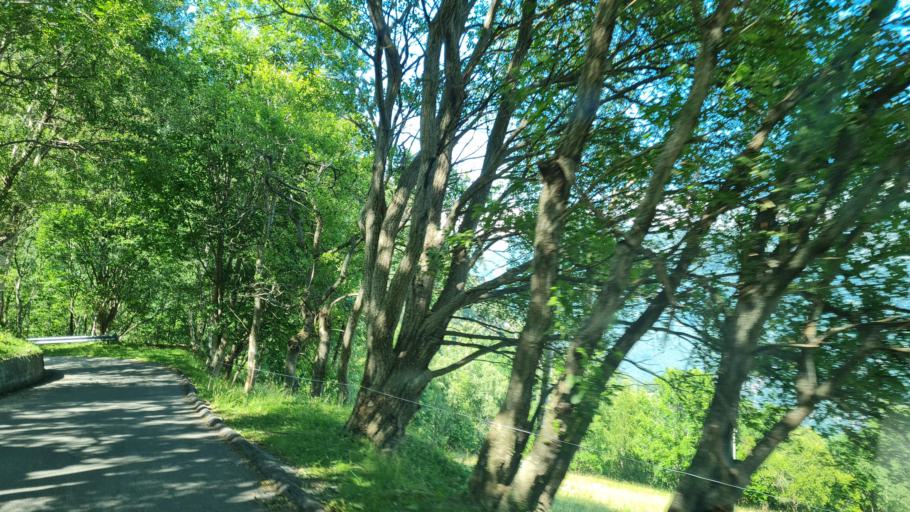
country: IT
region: Piedmont
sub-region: Provincia di Torino
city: Quincinetto
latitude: 45.5524
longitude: 7.7766
